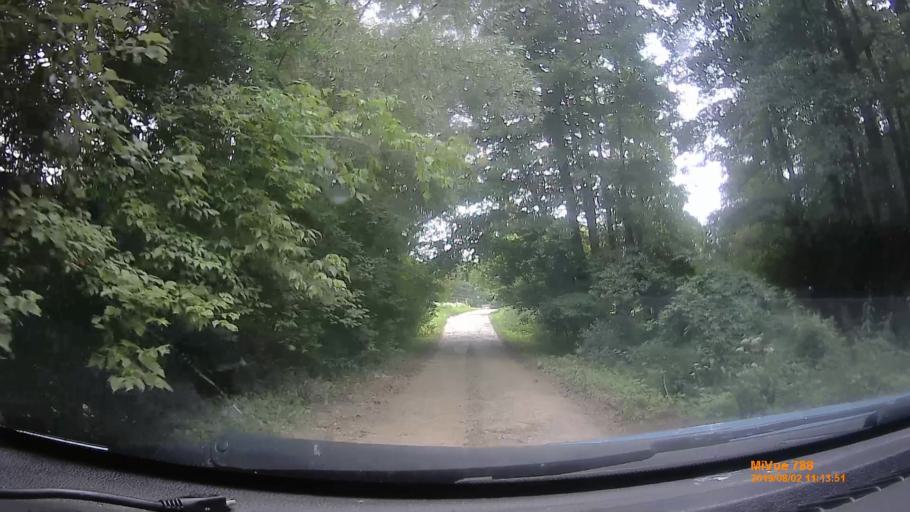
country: HU
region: Baranya
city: Buekkoesd
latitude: 46.1134
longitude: 17.9361
